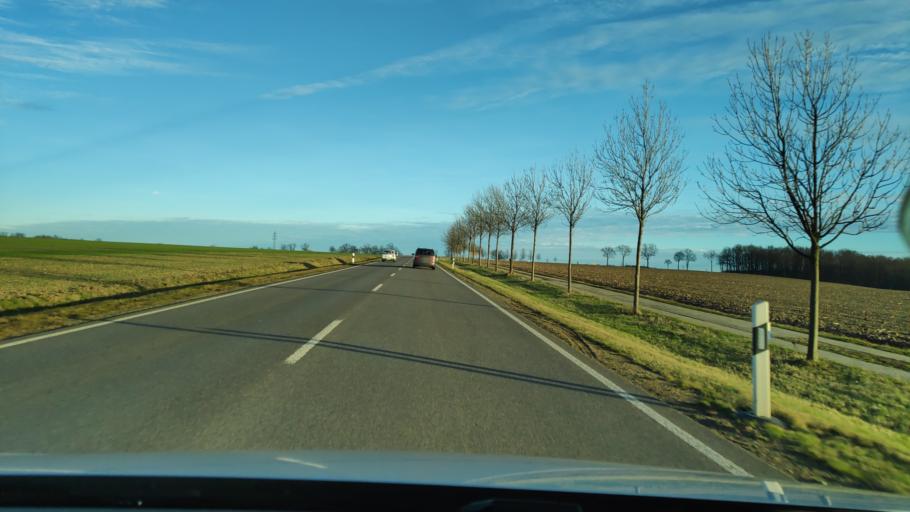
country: DE
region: Saxony
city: Mulsen
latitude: 50.7641
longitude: 12.5226
